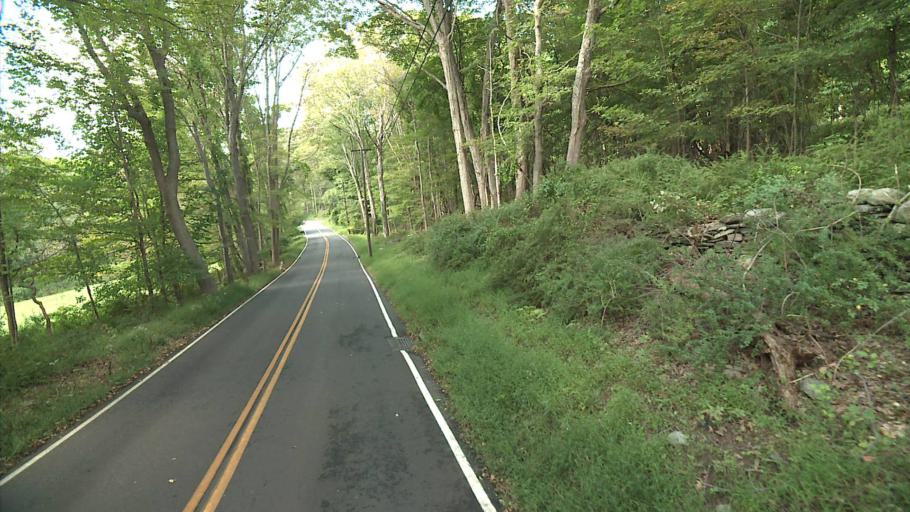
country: US
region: Connecticut
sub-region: Middlesex County
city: East Haddam
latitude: 41.4332
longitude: -72.4307
